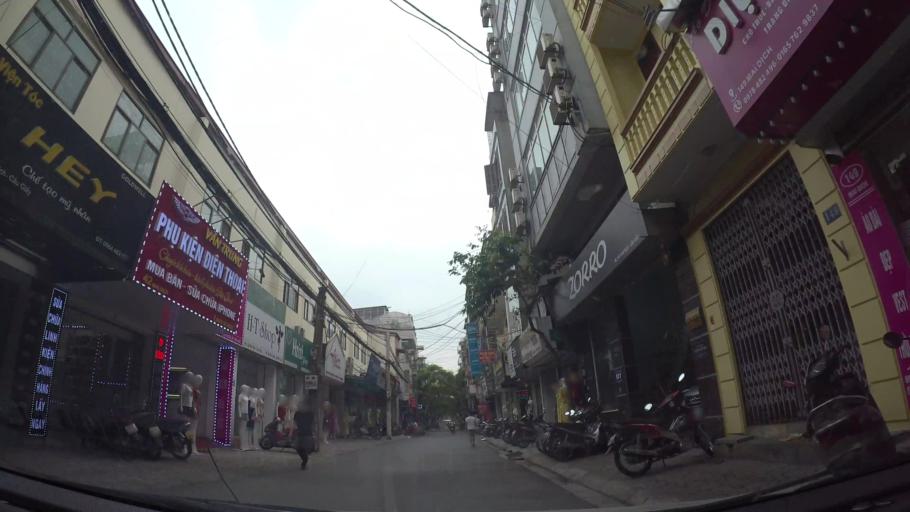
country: VN
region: Ha Noi
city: Cau Dien
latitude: 21.0404
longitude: 105.7746
